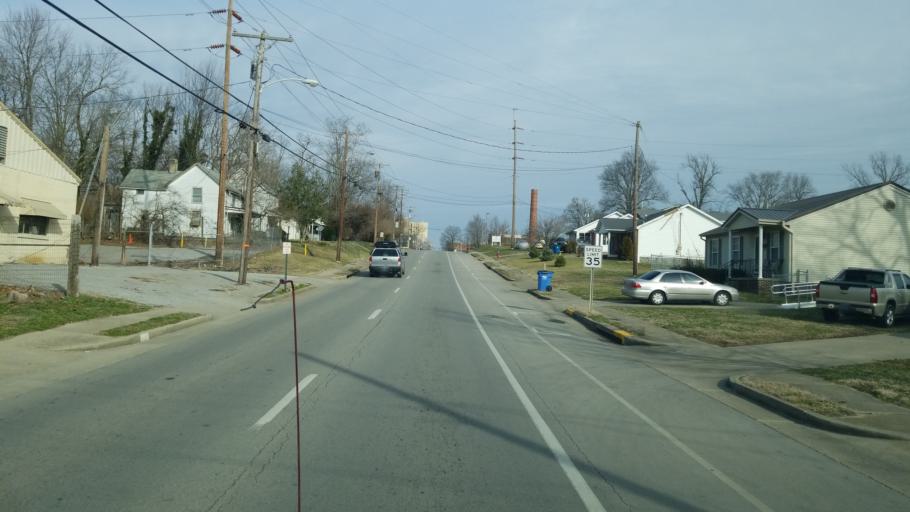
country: US
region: Kentucky
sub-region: Boyle County
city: Danville
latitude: 37.6390
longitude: -84.7731
